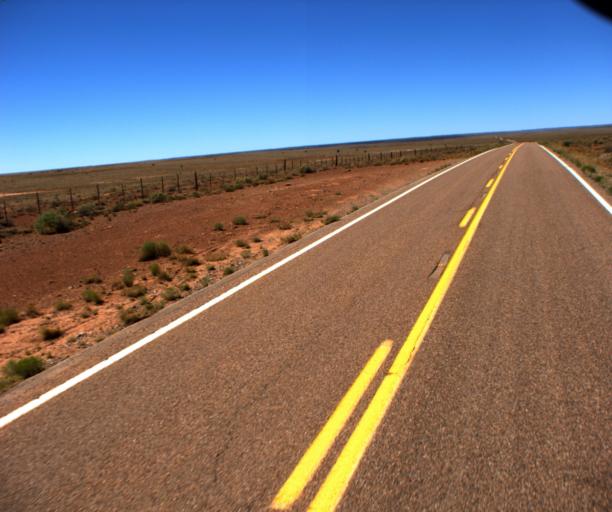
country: US
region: Arizona
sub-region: Navajo County
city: Winslow
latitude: 34.8637
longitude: -110.6601
